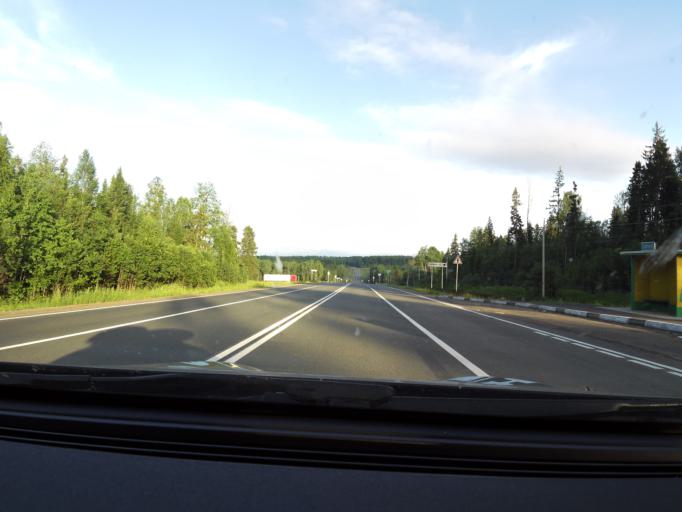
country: RU
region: Perm
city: Siva
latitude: 58.5495
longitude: 53.9082
